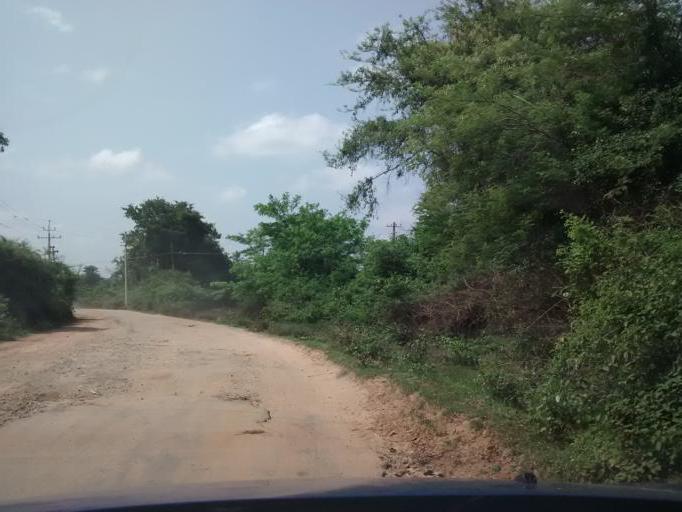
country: IN
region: Karnataka
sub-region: Hassan
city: Hole Narsipur
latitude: 12.6974
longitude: 76.1661
